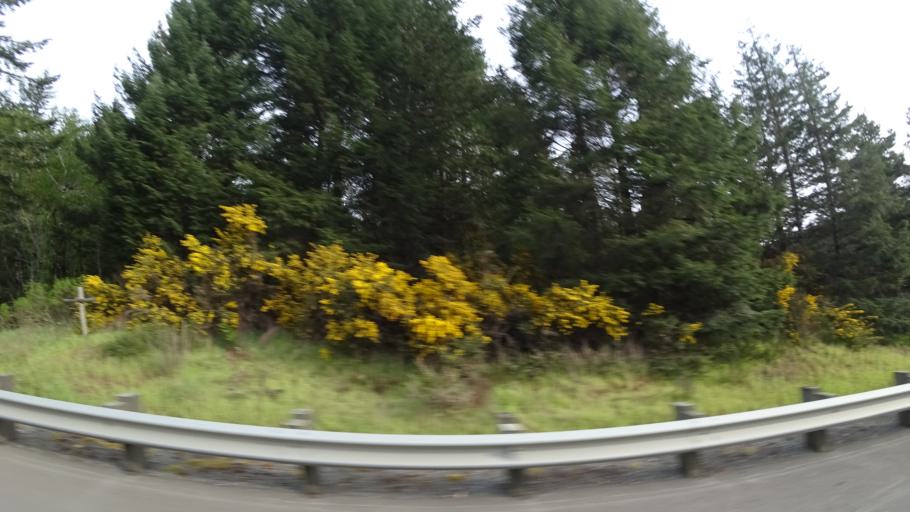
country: US
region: Oregon
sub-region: Coos County
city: Bandon
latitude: 43.1929
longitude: -124.3473
